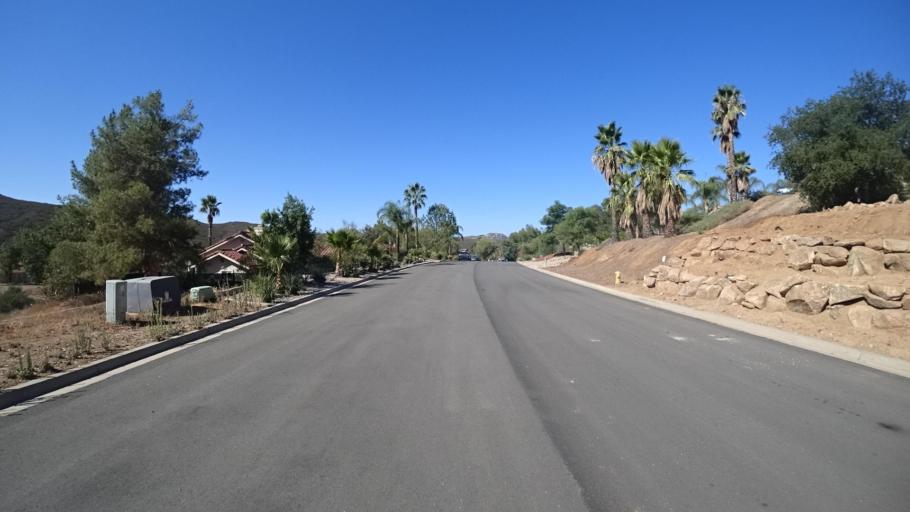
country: US
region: California
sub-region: San Diego County
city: San Diego Country Estates
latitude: 33.0015
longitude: -116.7618
